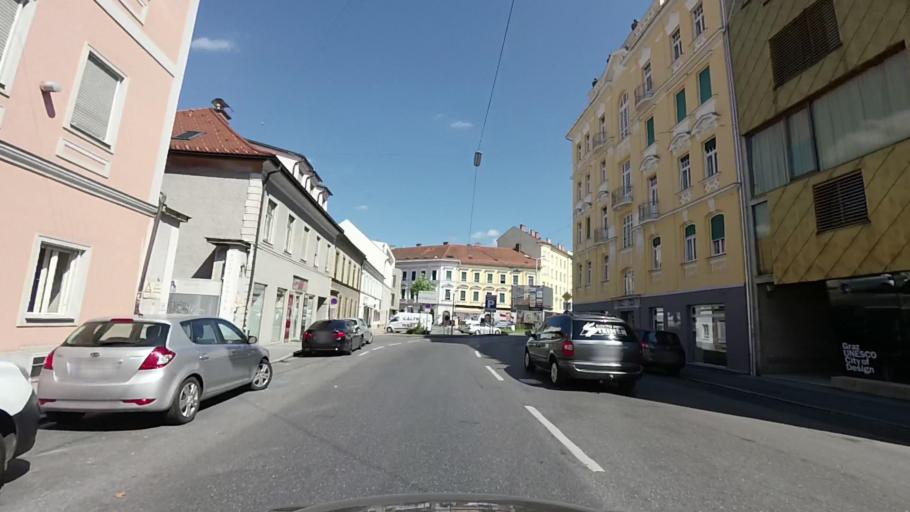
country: AT
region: Styria
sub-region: Graz Stadt
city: Graz
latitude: 47.0645
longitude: 15.4401
